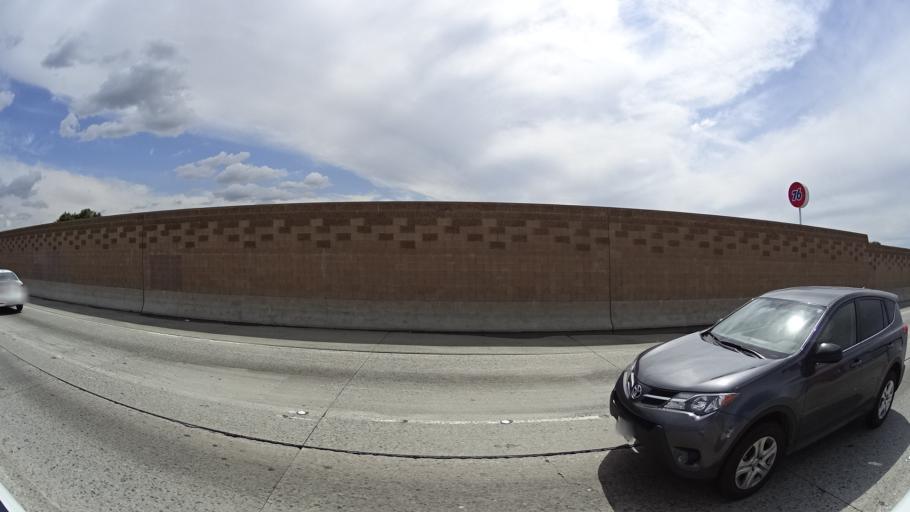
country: US
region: California
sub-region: Los Angeles County
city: El Monte
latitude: 34.0686
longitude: -118.0420
